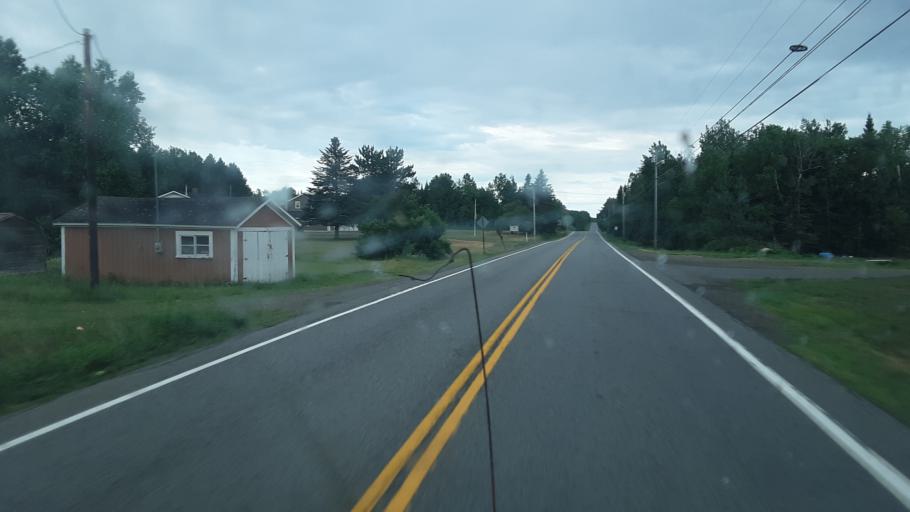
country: US
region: Maine
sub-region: Aroostook County
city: Presque Isle
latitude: 46.4947
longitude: -68.3729
